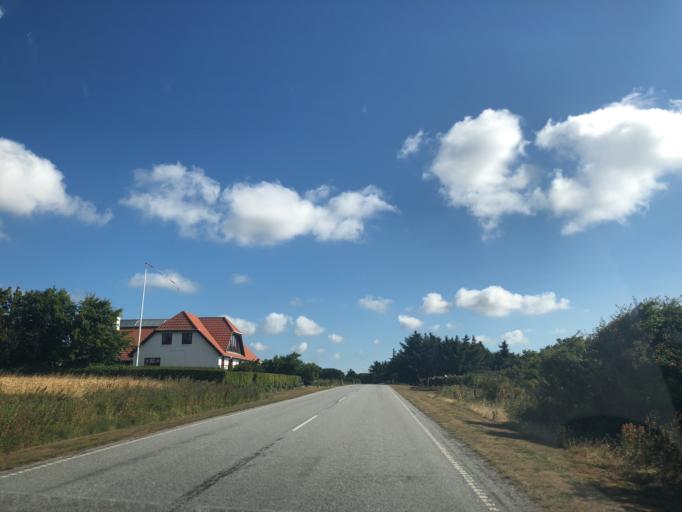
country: DK
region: North Denmark
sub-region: Morso Kommune
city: Nykobing Mors
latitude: 56.9880
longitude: 8.9127
